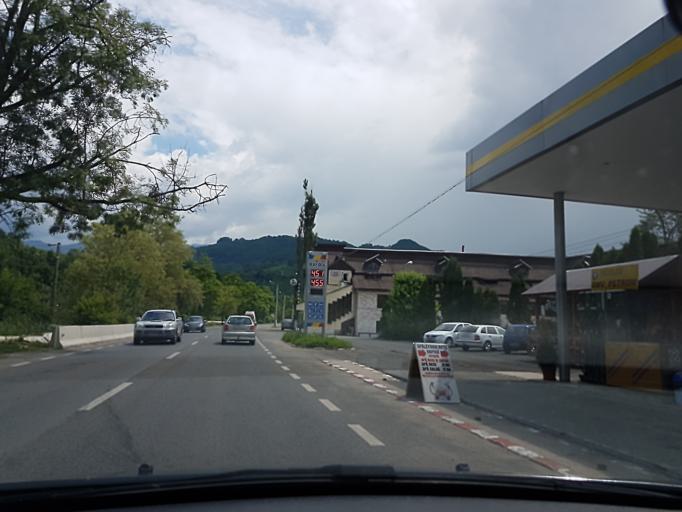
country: RO
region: Hunedoara
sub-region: Comuna Aninoasa
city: Iscroni
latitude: 45.3732
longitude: 23.3565
